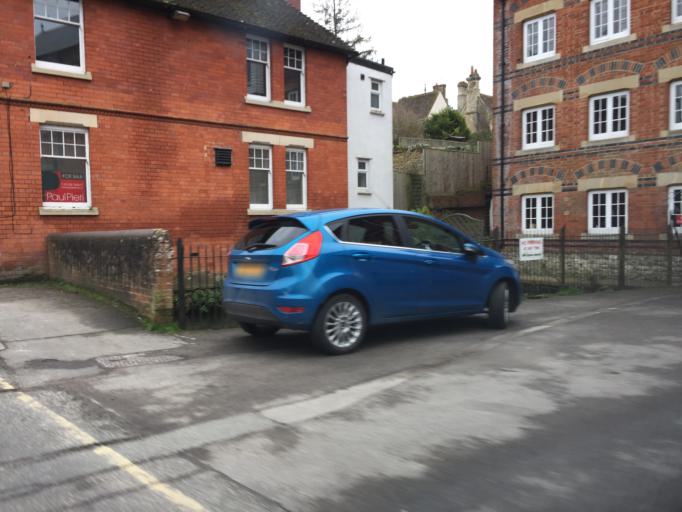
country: GB
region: England
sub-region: Oxfordshire
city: Wantage
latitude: 51.5899
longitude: -1.4287
